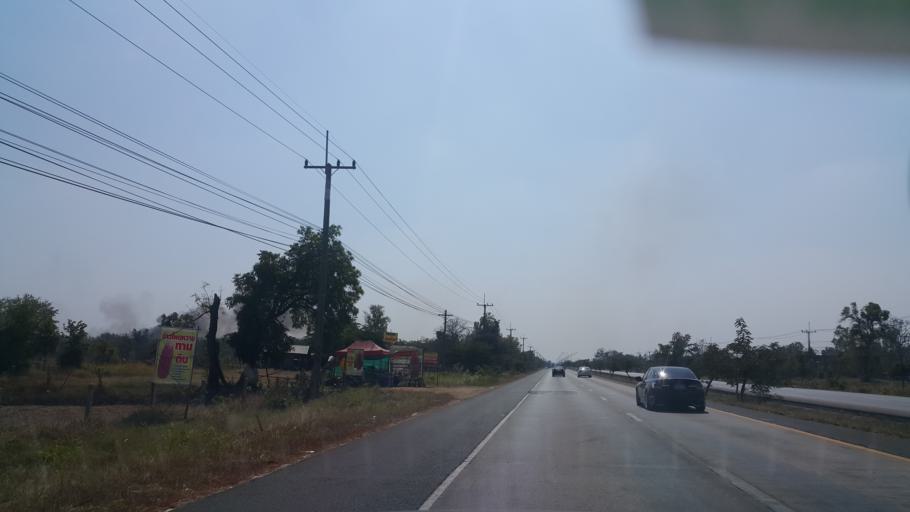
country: TH
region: Nakhon Ratchasima
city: Sida
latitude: 15.4936
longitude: 102.5241
